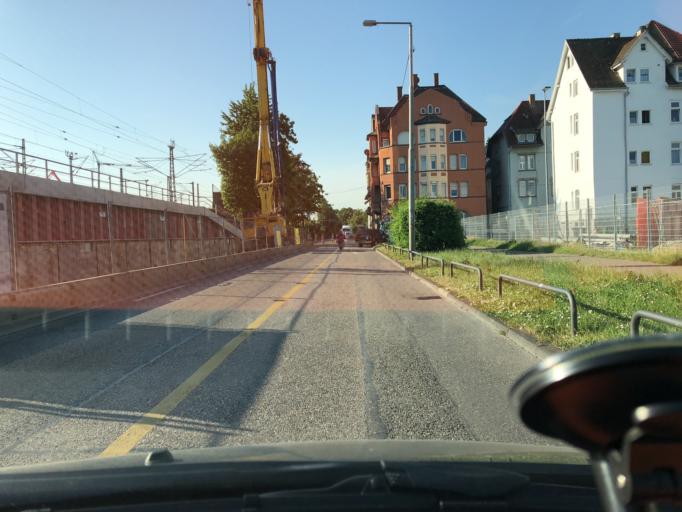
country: DE
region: Baden-Wuerttemberg
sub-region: Regierungsbezirk Stuttgart
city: Stuttgart-Ost
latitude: 48.7836
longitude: 9.2470
